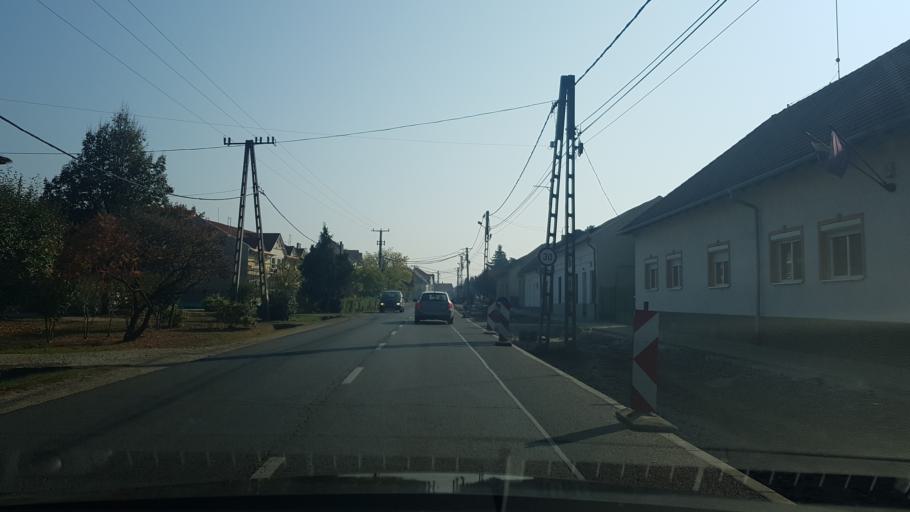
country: HU
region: Fejer
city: Adony
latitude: 47.1206
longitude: 18.8635
